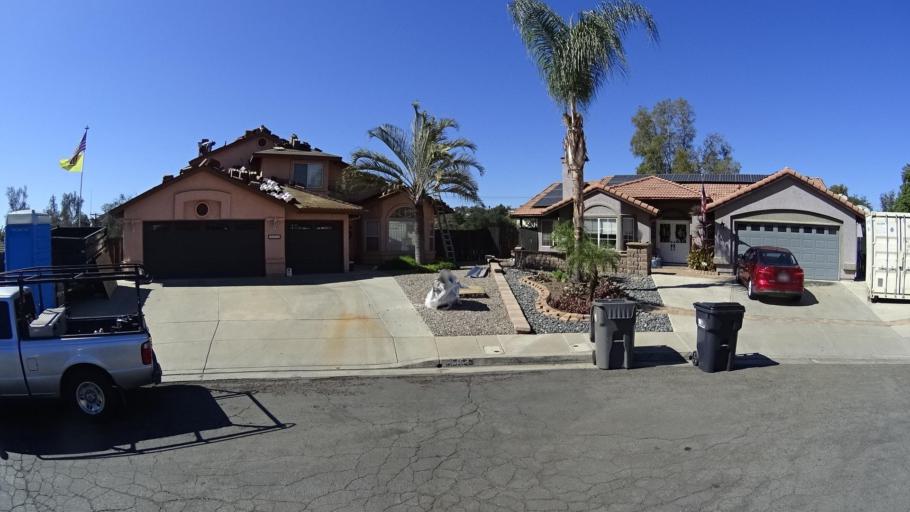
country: US
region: California
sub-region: San Diego County
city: Crest
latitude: 32.8505
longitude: -116.8669
